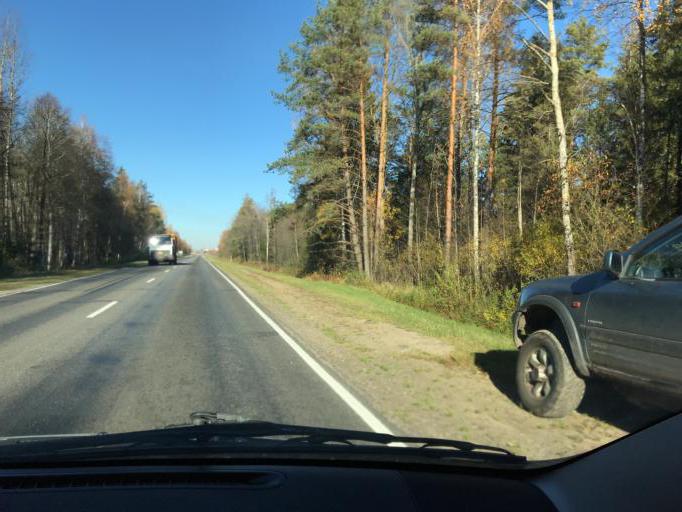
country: BY
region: Vitebsk
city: Polatsk
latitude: 55.4425
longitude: 28.7750
